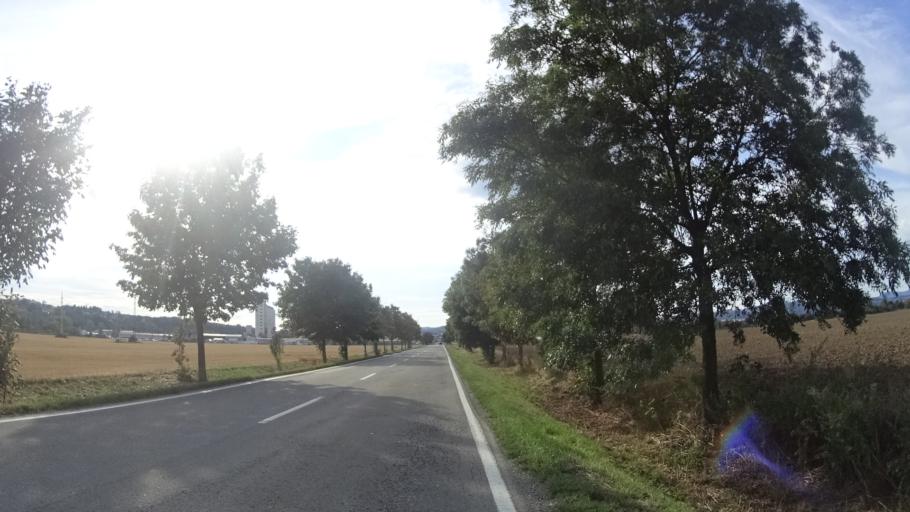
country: CZ
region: Olomoucky
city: Lestina
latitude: 49.8740
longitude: 16.9020
